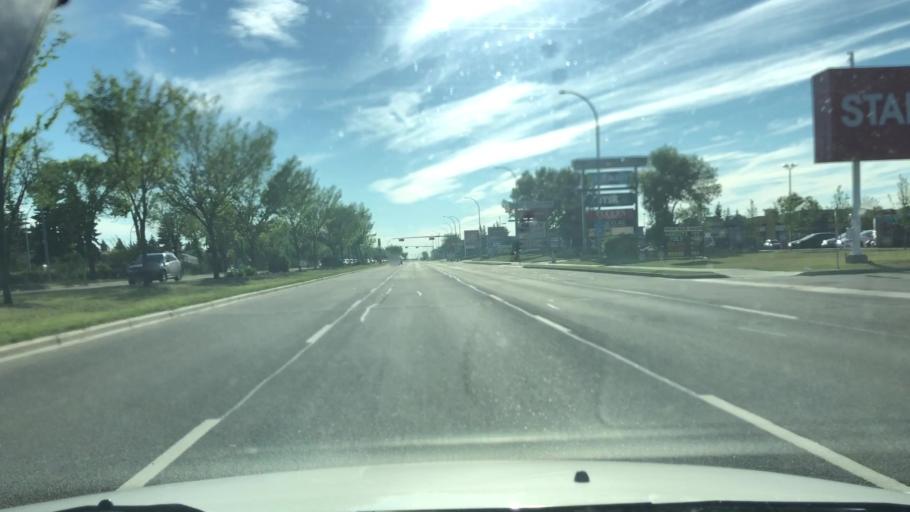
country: CA
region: Alberta
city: Edmonton
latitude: 53.5996
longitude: -113.5477
